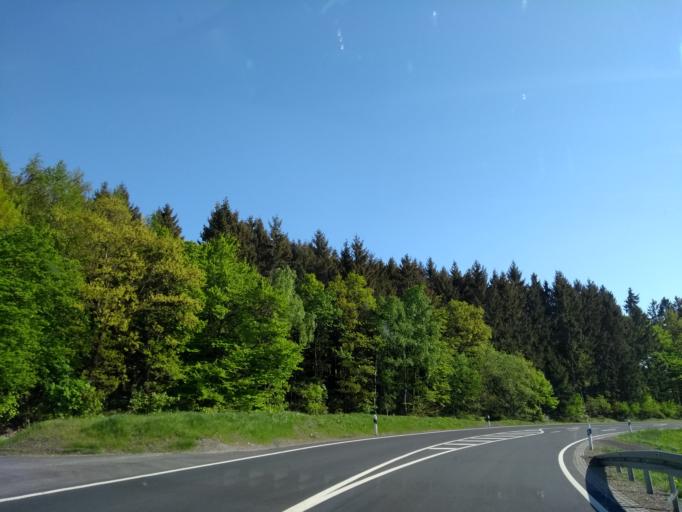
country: DE
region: Hesse
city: Battenberg
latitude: 50.9759
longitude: 8.6127
